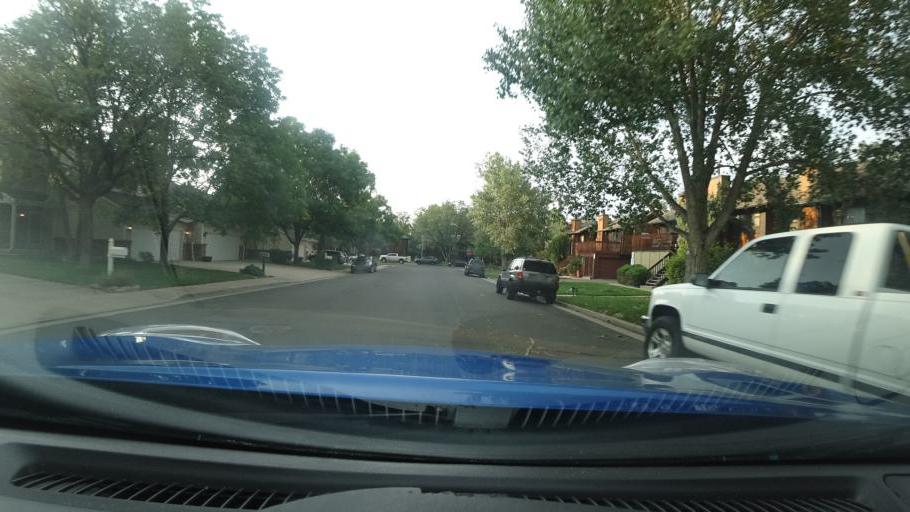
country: US
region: Colorado
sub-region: Adams County
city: Aurora
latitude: 39.6937
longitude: -104.8227
